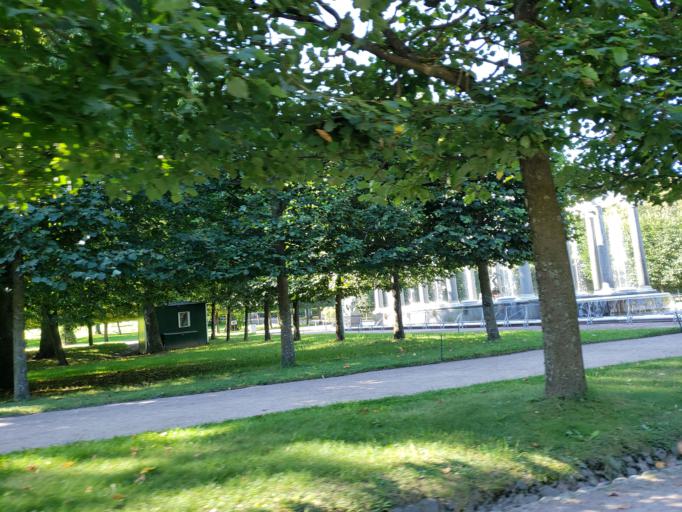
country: RU
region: St.-Petersburg
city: Peterhof
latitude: 59.8877
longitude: 29.9031
